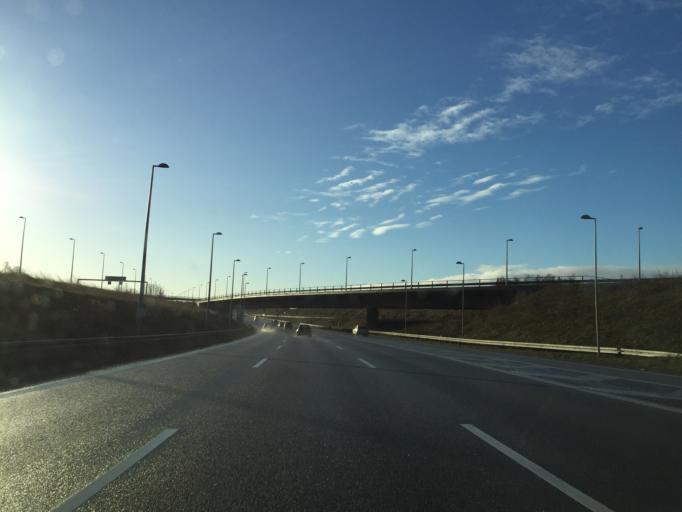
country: DK
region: Capital Region
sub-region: Rodovre Kommune
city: Rodovre
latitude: 55.6886
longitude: 12.4312
